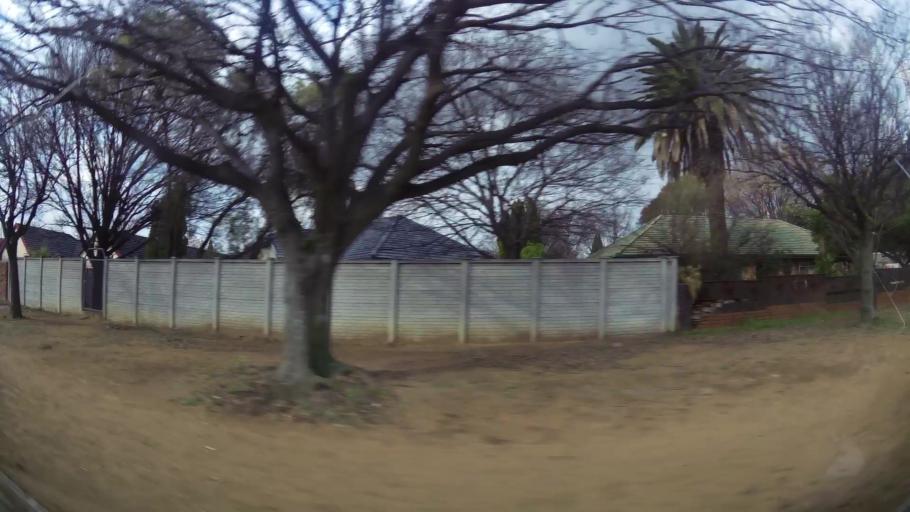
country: ZA
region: Orange Free State
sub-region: Fezile Dabi District Municipality
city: Sasolburg
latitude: -26.8155
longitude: 27.8301
